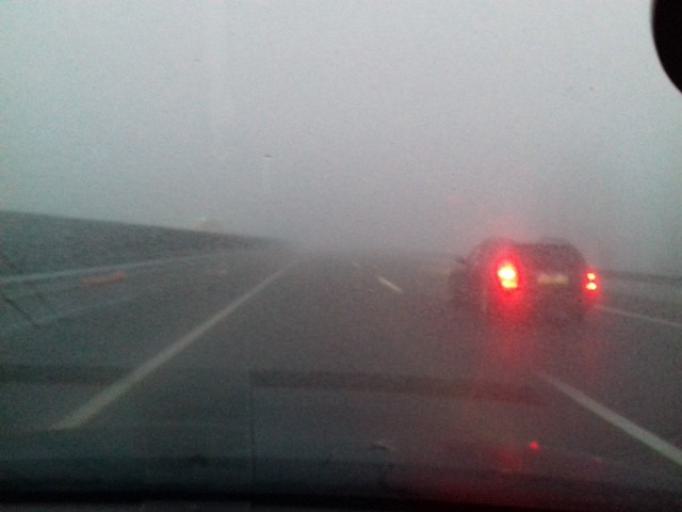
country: HU
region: Hajdu-Bihar
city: Hajdunanas
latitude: 47.8863
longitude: 21.4430
